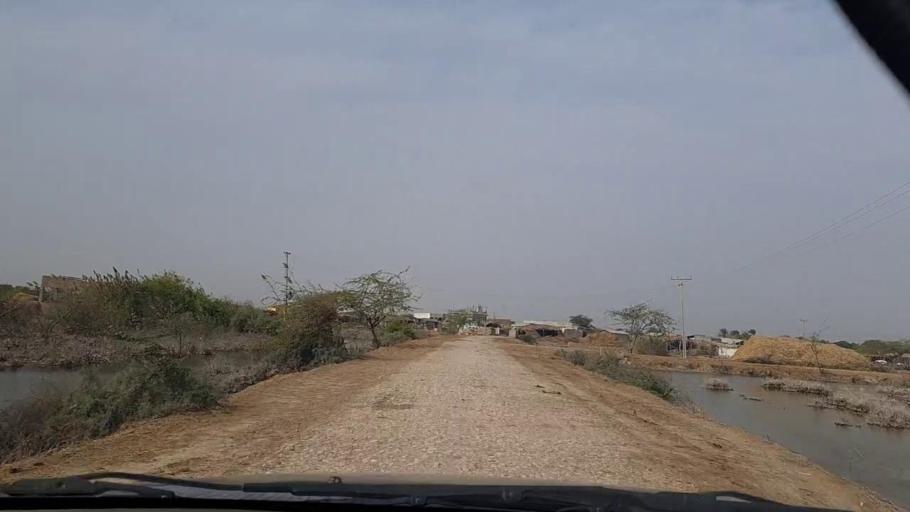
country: PK
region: Sindh
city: Thatta
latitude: 24.5863
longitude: 67.9075
